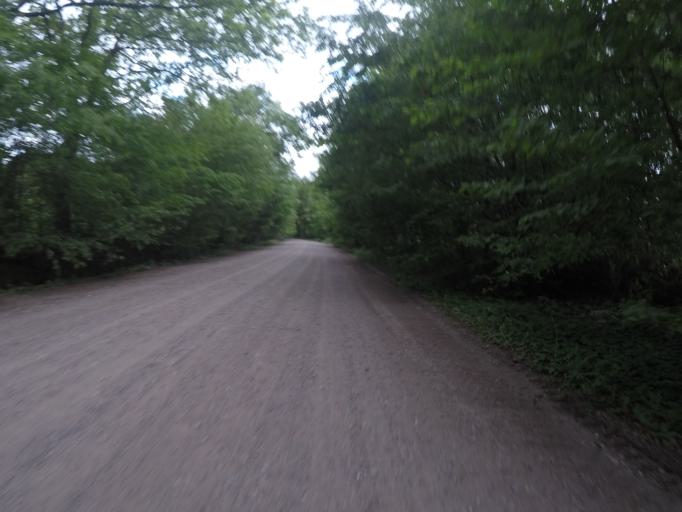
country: DE
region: Schleswig-Holstein
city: Quickborn
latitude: 53.7113
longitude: 9.9176
